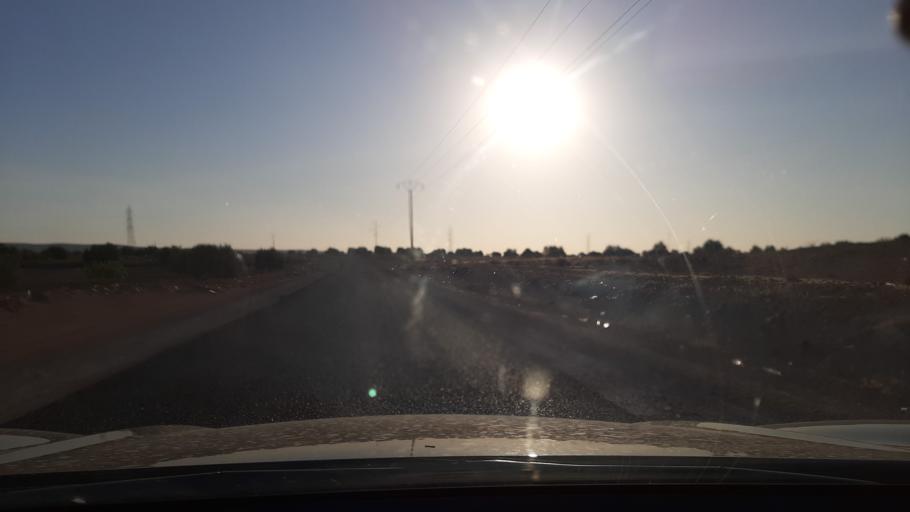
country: TN
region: Qabis
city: Matmata
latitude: 33.6171
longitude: 10.2377
